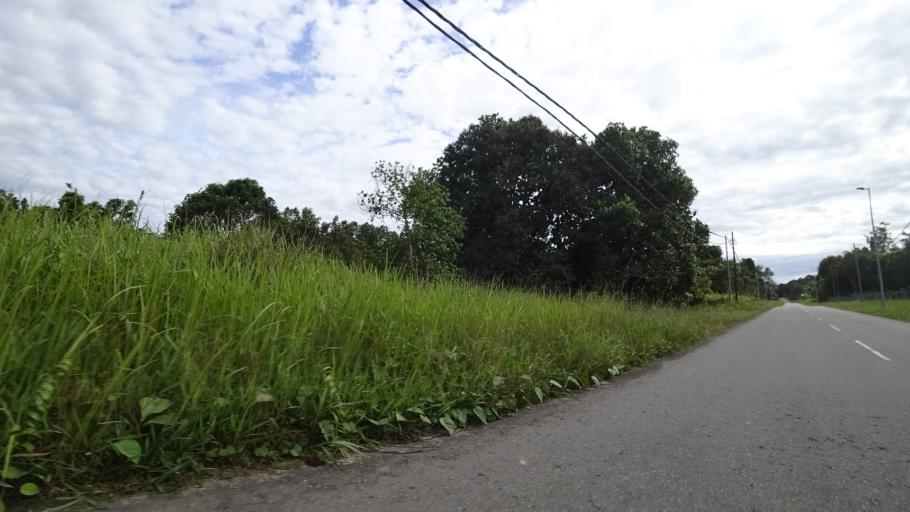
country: BN
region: Brunei and Muara
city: Bandar Seri Begawan
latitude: 4.8393
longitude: 114.9514
